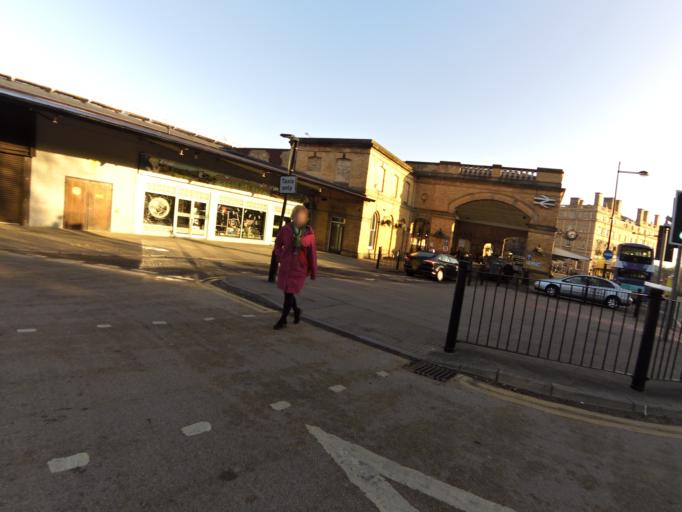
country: GB
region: England
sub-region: City of York
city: York
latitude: 53.9575
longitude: -1.0923
